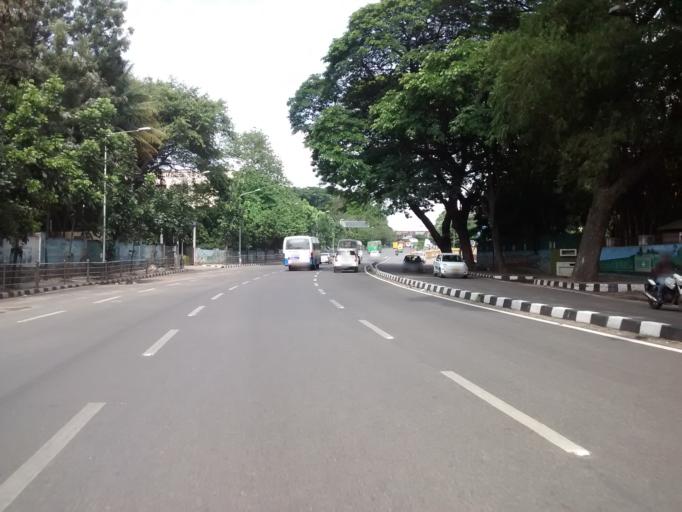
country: IN
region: Karnataka
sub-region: Bangalore Urban
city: Bangalore
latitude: 12.9802
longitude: 77.5808
